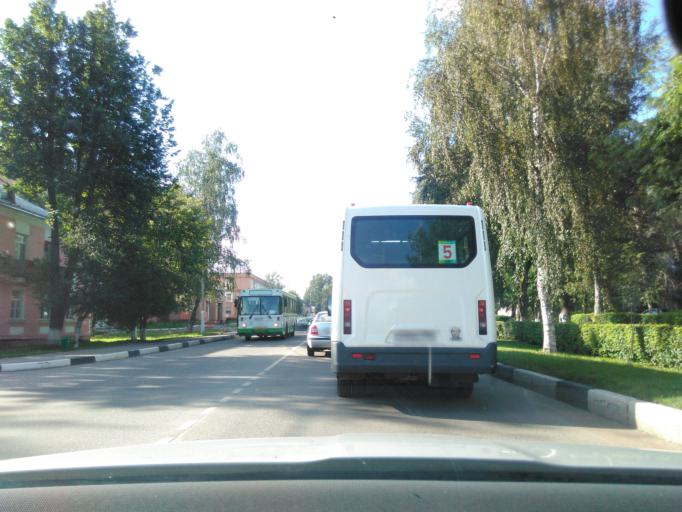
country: RU
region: Moskovskaya
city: Klin
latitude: 56.3228
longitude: 36.7208
